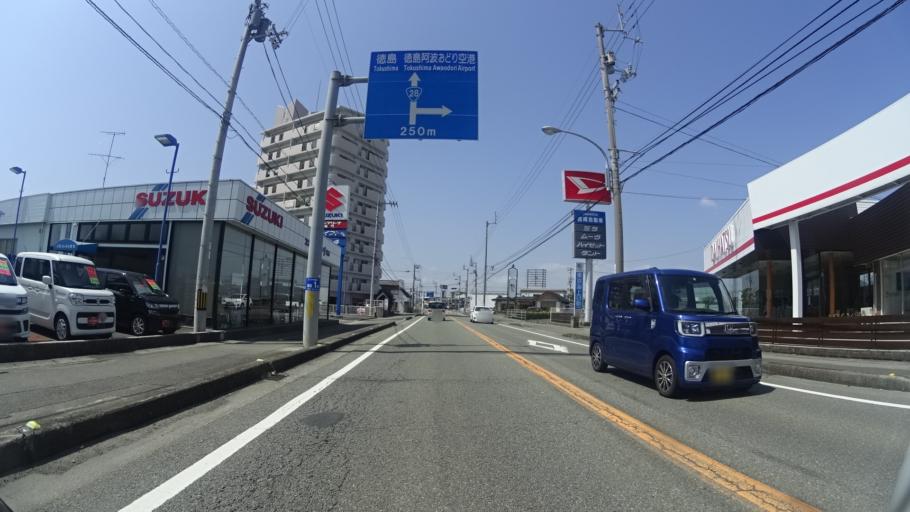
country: JP
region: Tokushima
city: Narutocho-mitsuishi
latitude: 34.1627
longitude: 134.5946
